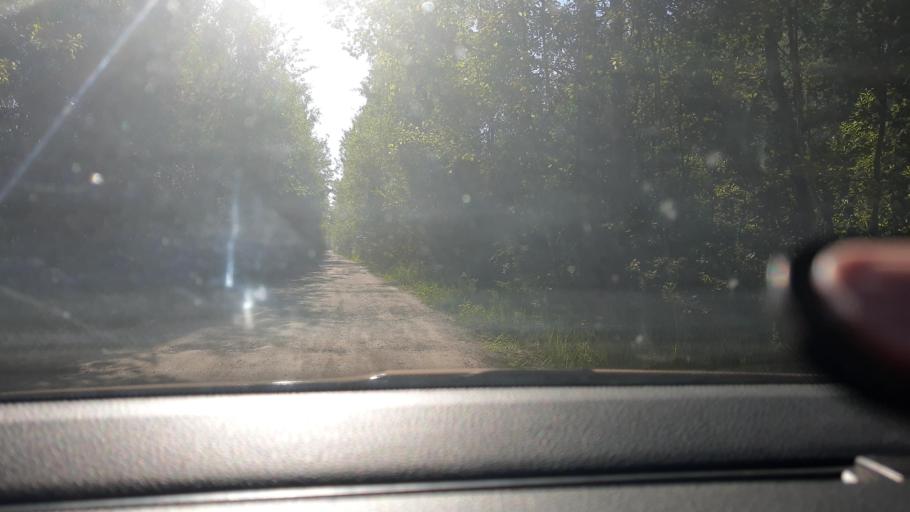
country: RU
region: Moskovskaya
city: Elektrogorsk
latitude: 55.8936
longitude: 38.7191
